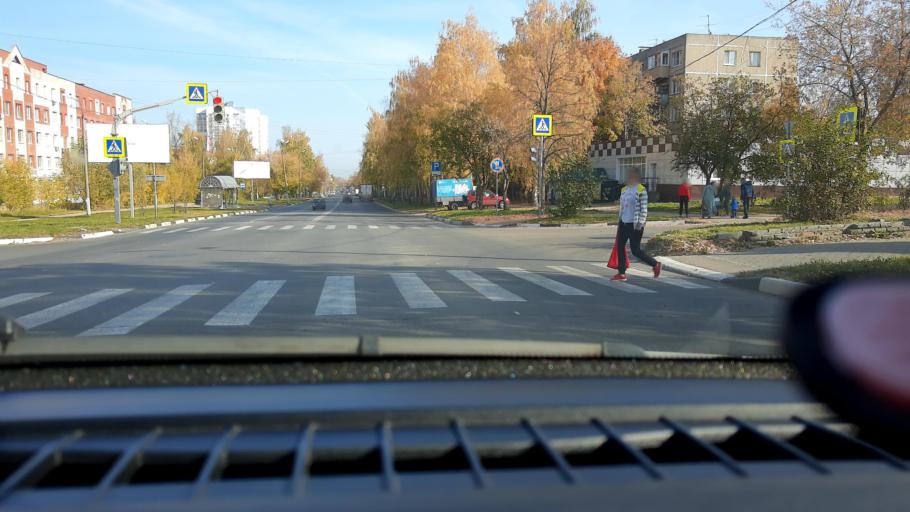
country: RU
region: Nizjnij Novgorod
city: Kstovo
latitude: 56.1483
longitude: 44.1820
